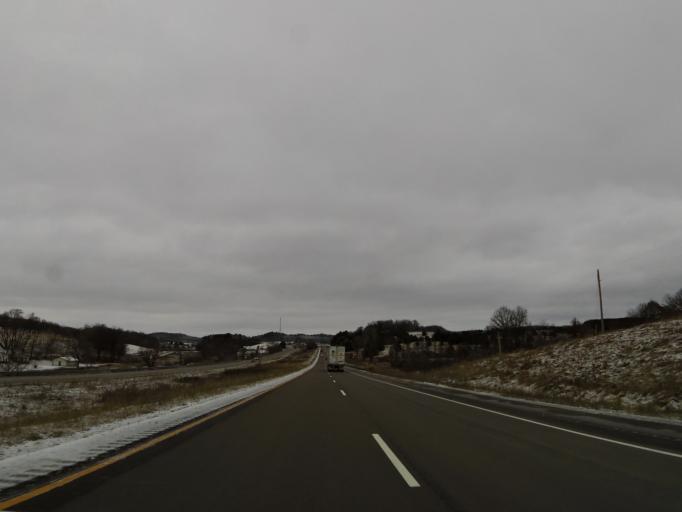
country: US
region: Wisconsin
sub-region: Trempealeau County
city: Osseo
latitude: 44.4848
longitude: -91.1173
